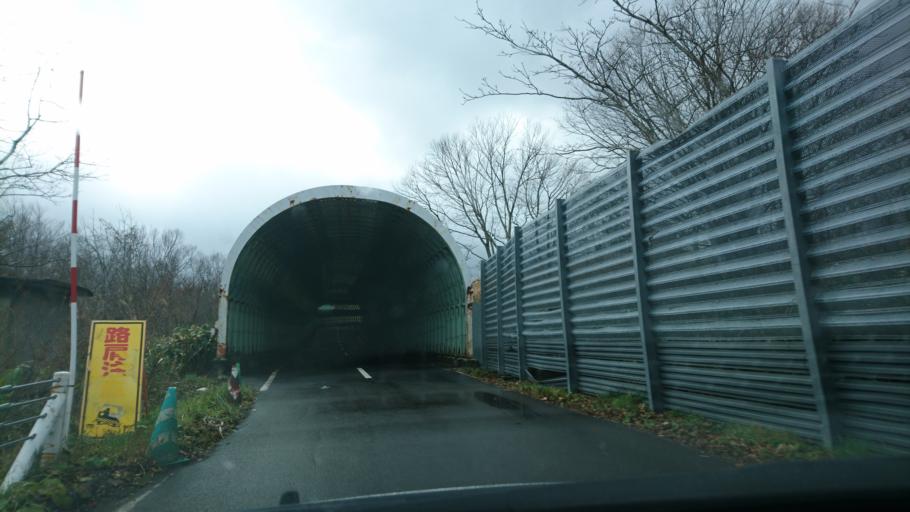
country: JP
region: Iwate
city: Ichinoseki
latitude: 38.9391
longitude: 140.8245
